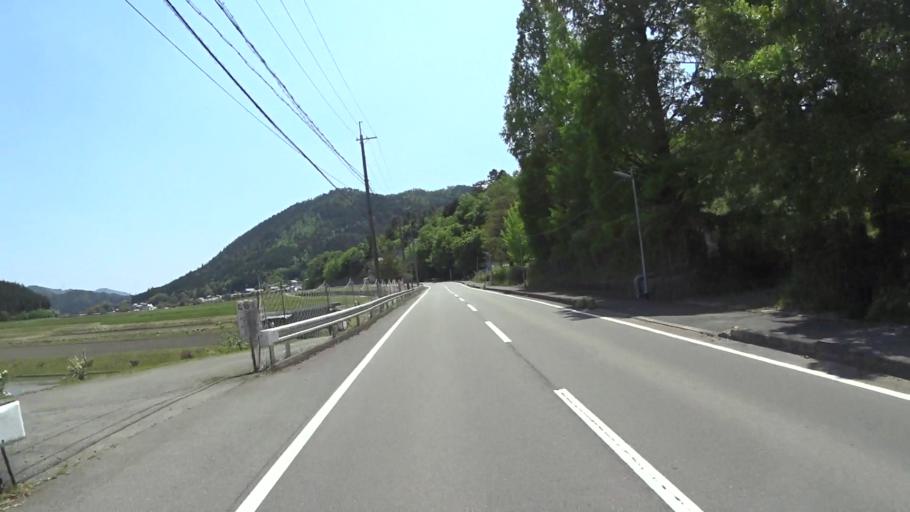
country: JP
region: Kyoto
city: Kameoka
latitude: 35.0326
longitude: 135.4844
